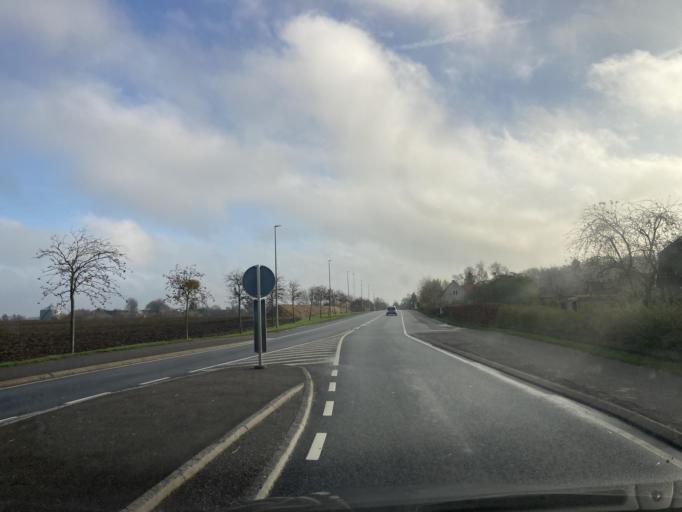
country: DK
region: Zealand
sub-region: Lolland Kommune
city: Maribo
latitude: 54.8088
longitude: 11.4221
